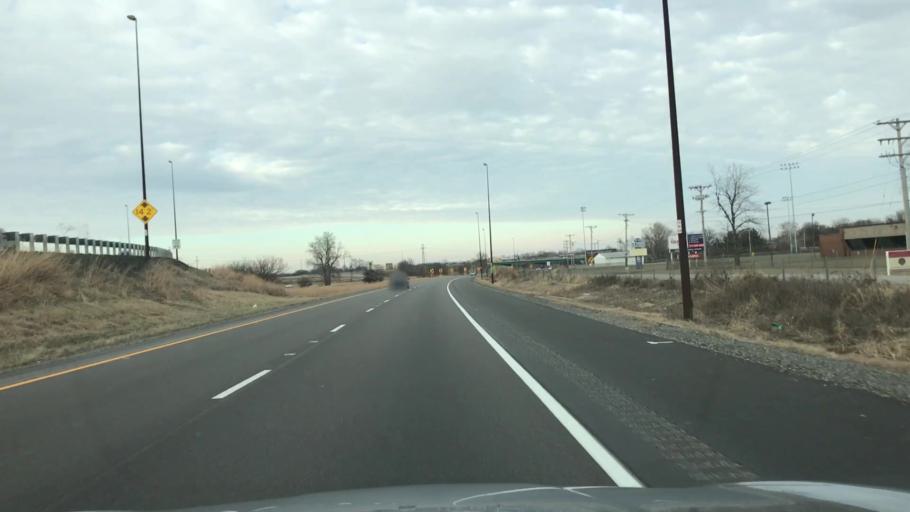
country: US
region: Illinois
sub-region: Sangamon County
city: Southern View
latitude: 39.7368
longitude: -89.6433
